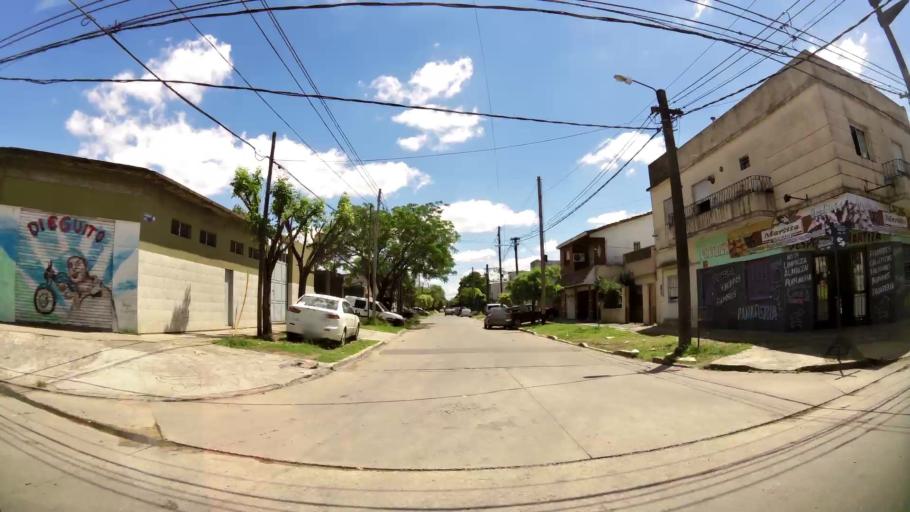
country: AR
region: Buenos Aires
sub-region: Partido de Lomas de Zamora
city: Lomas de Zamora
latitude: -34.7359
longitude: -58.4178
